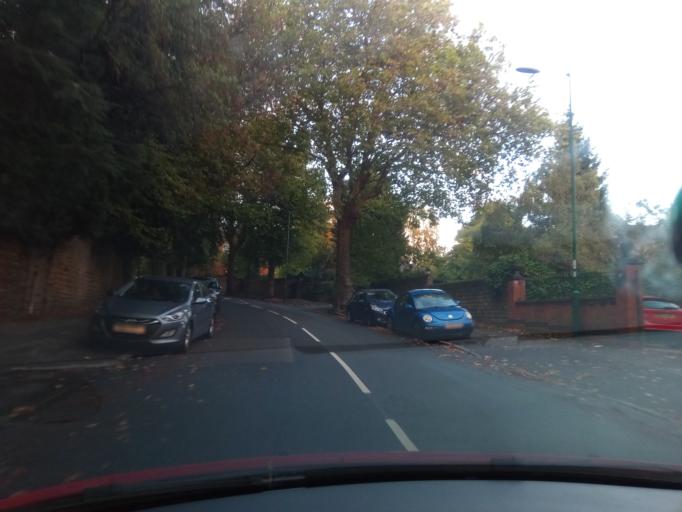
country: GB
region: England
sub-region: Nottingham
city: Nottingham
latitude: 52.9702
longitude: -1.1466
